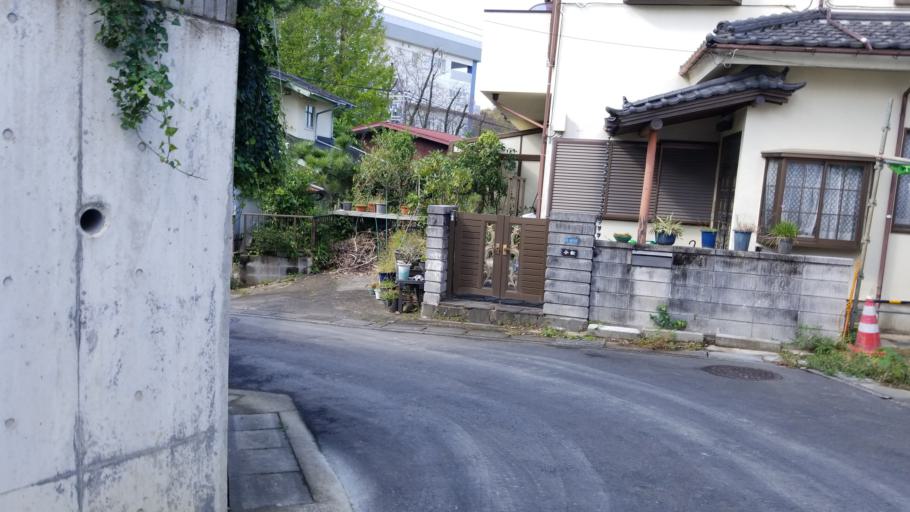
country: JP
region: Tokyo
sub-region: Machida-shi
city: Machida
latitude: 35.5868
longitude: 139.5010
